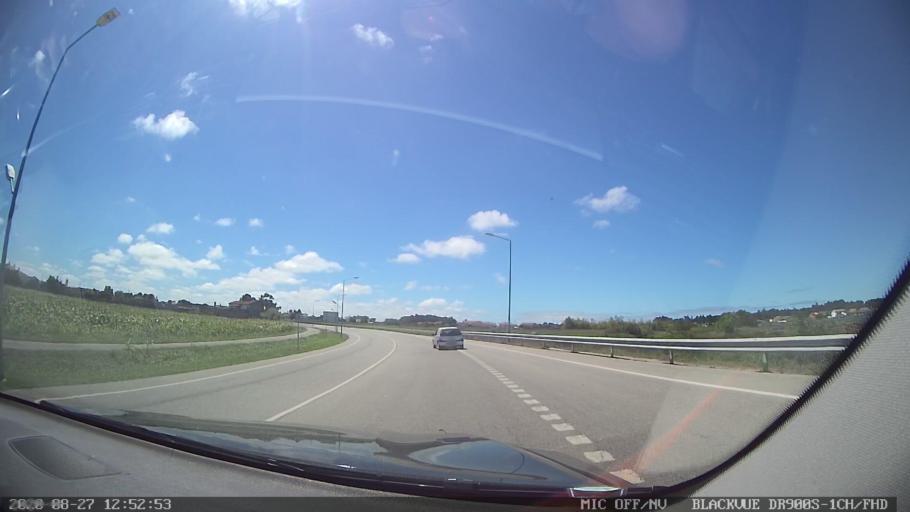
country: PT
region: Aveiro
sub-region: Ilhavo
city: Ilhavo
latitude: 40.6056
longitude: -8.6806
